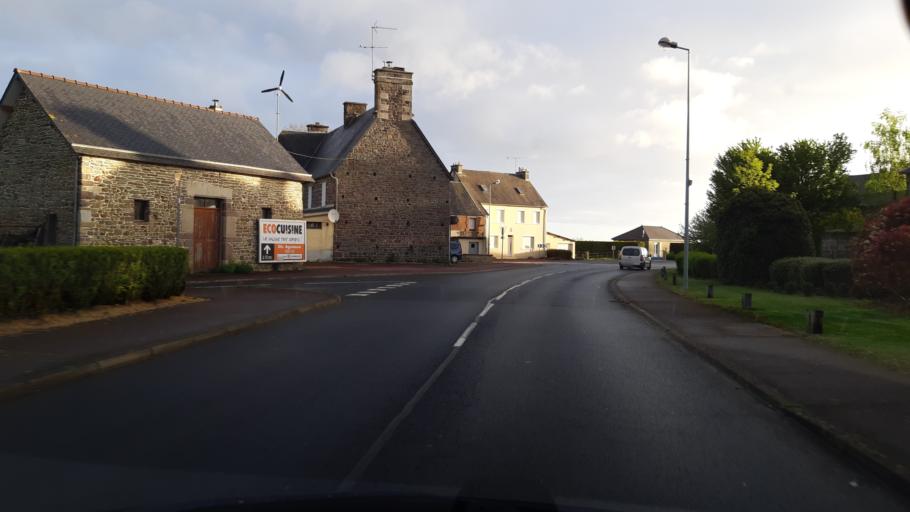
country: FR
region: Lower Normandy
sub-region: Departement de la Manche
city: Agneaux
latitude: 49.0273
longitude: -1.1448
